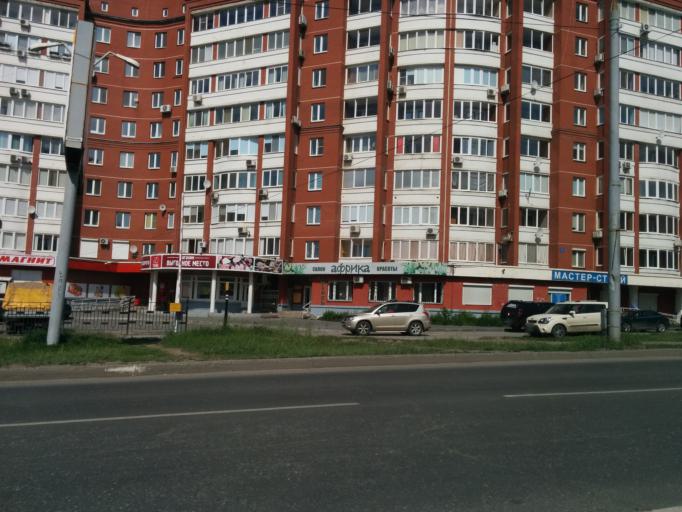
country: RU
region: Perm
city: Perm
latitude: 58.0072
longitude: 56.3015
